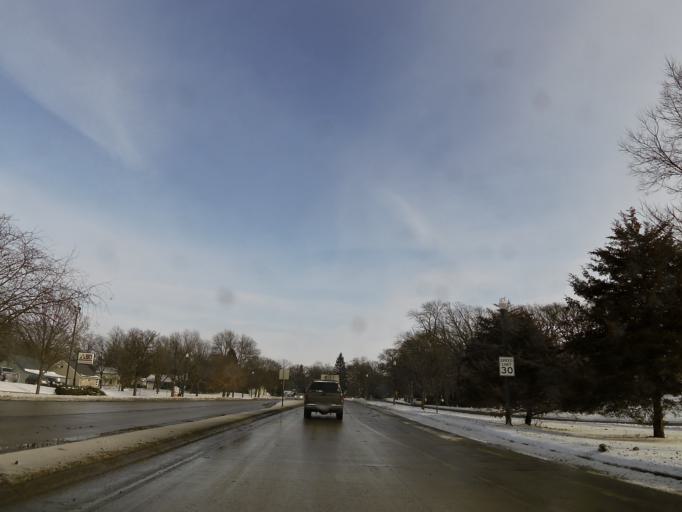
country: US
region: Minnesota
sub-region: McLeod County
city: Hutchinson
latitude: 44.8808
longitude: -94.3724
